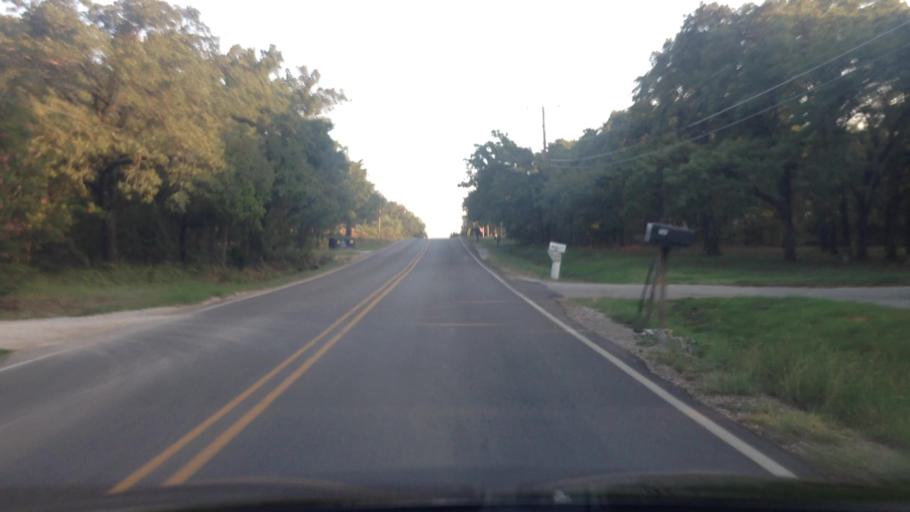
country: US
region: Texas
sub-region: Tarrant County
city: Rendon
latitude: 32.6050
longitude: -97.2154
